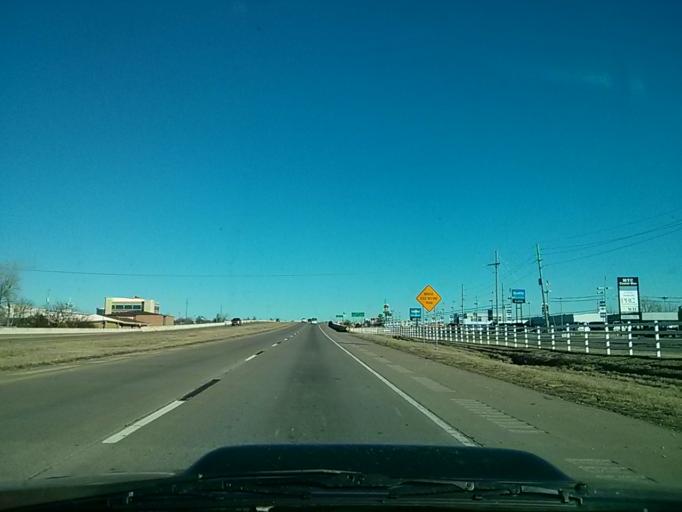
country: US
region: Oklahoma
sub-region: Tulsa County
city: Owasso
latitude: 36.2743
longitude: -95.8481
